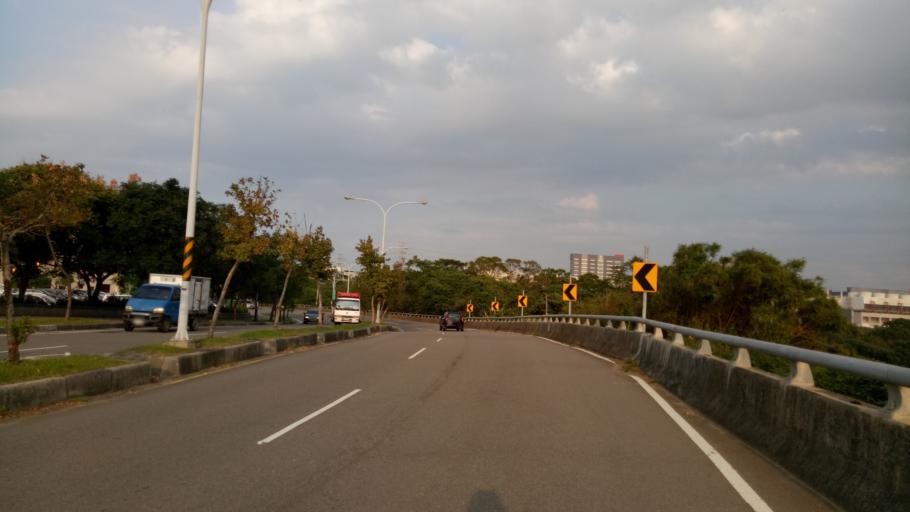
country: TW
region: Taiwan
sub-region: Hsinchu
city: Hsinchu
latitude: 24.7691
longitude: 121.0045
